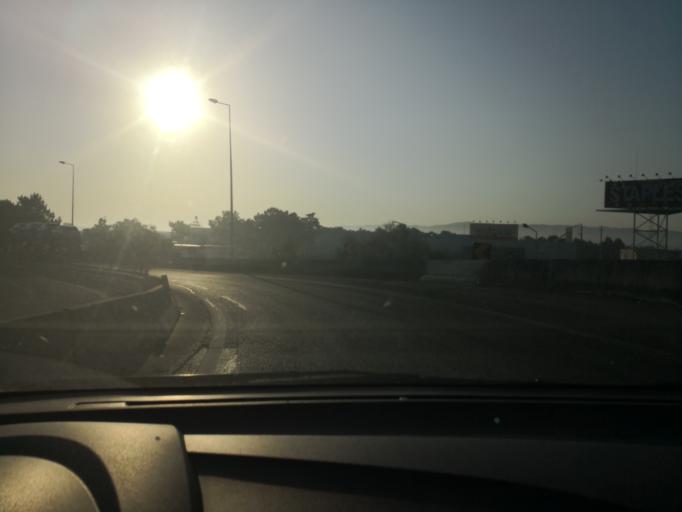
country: PT
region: Setubal
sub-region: Barreiro
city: Santo Antonio da Charneca
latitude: 38.5777
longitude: -9.0163
